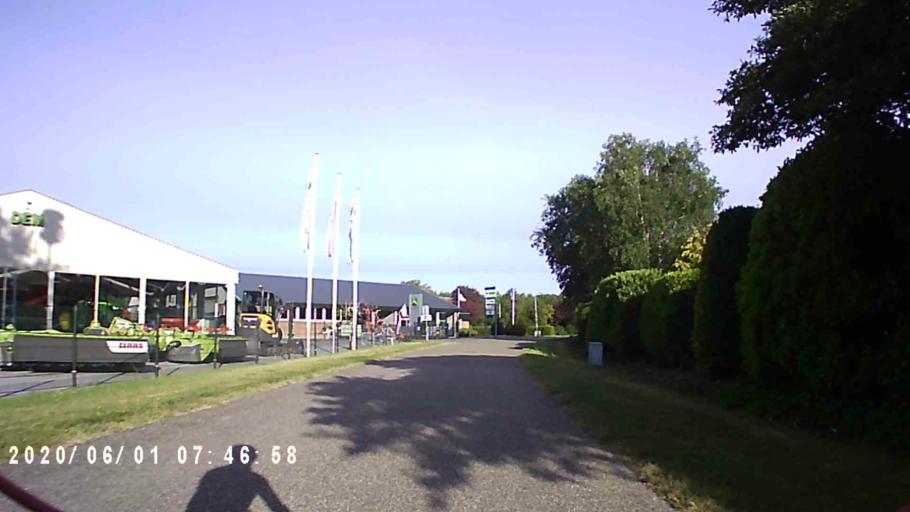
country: NL
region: Friesland
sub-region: Gemeente Dantumadiel
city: Rinsumageast
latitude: 53.2951
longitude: 5.9546
